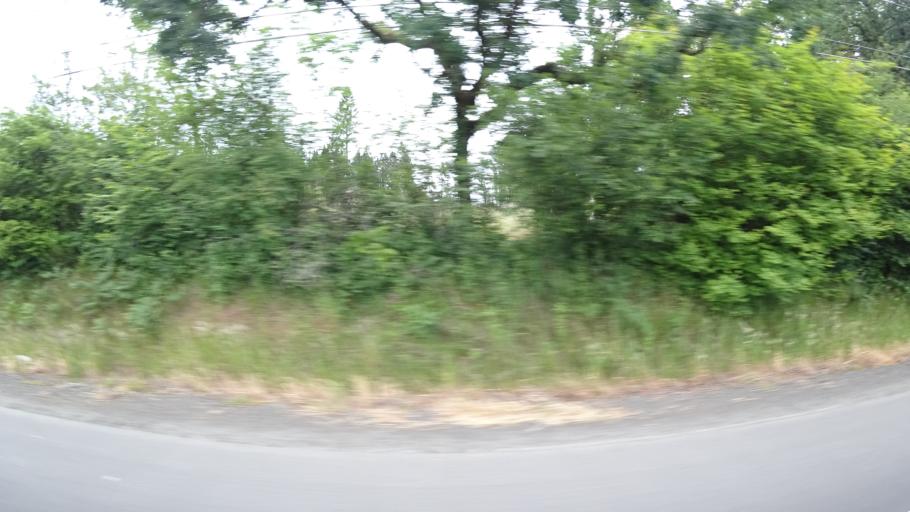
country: US
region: Oregon
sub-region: Washington County
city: Hillsboro
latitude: 45.4842
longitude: -122.9361
